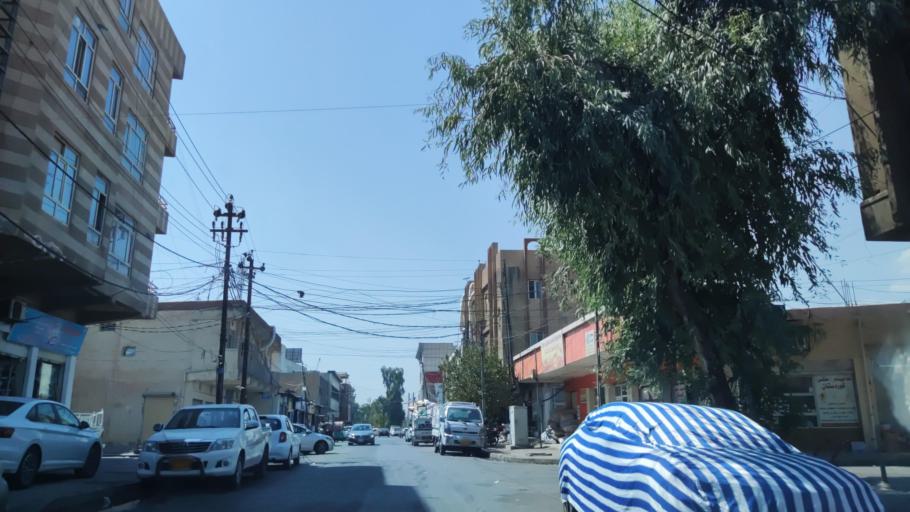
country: IQ
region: Arbil
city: Erbil
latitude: 36.1880
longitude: 44.0214
